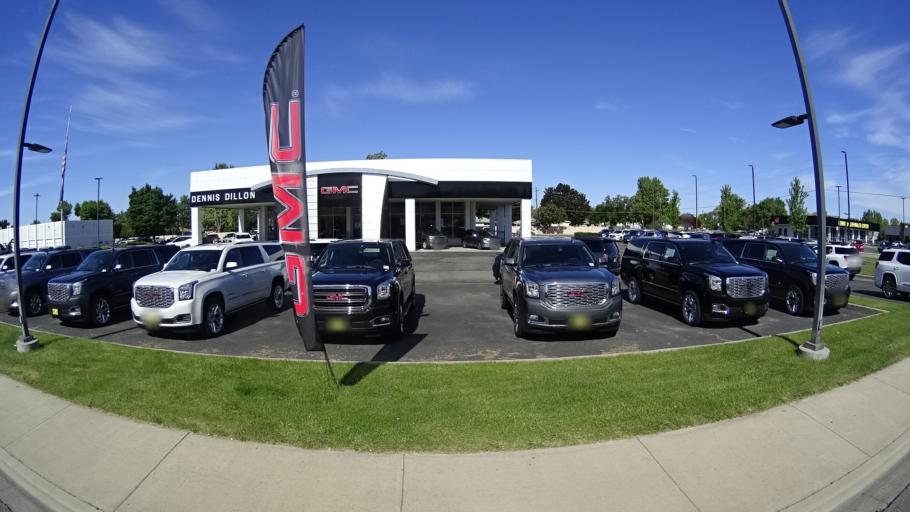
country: US
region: Idaho
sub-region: Ada County
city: Garden City
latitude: 43.5785
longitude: -116.2436
